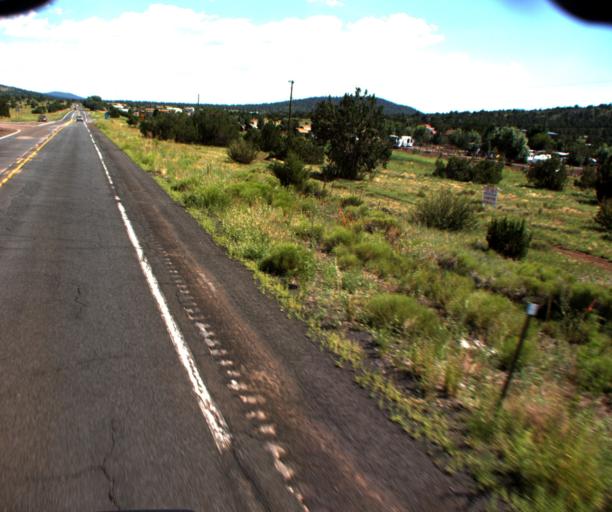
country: US
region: Arizona
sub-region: Coconino County
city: Williams
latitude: 35.3305
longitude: -112.1571
